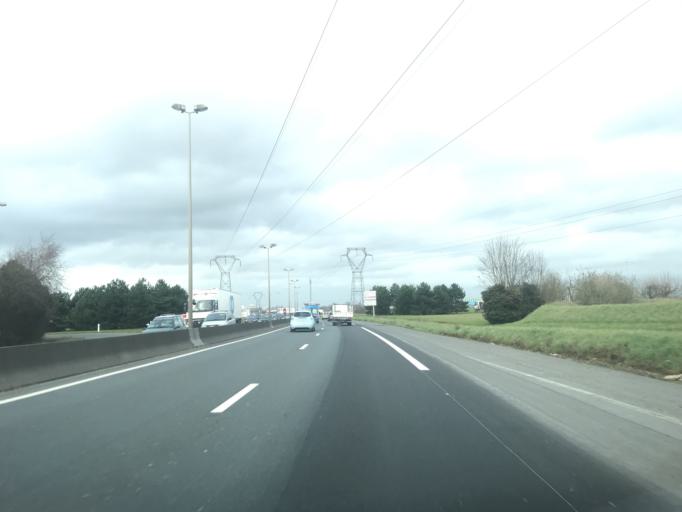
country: FR
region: Lower Normandy
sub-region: Departement du Calvados
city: Cormelles-le-Royal
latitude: 49.1491
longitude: -0.3200
